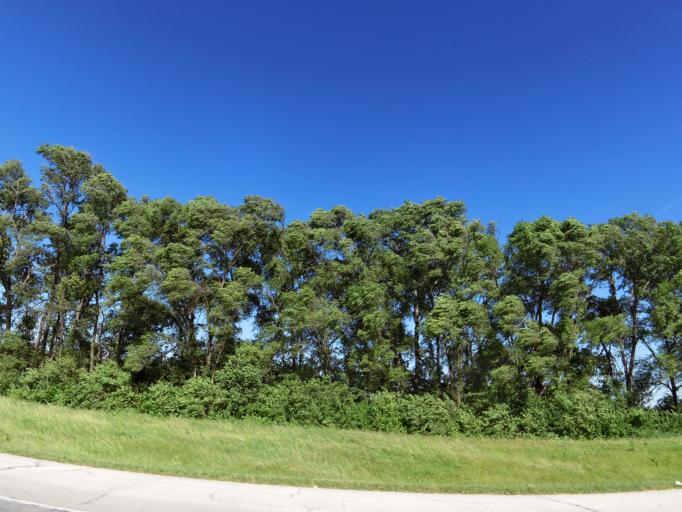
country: US
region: Illinois
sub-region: Winnebago County
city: South Beloit
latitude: 42.4693
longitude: -89.0194
